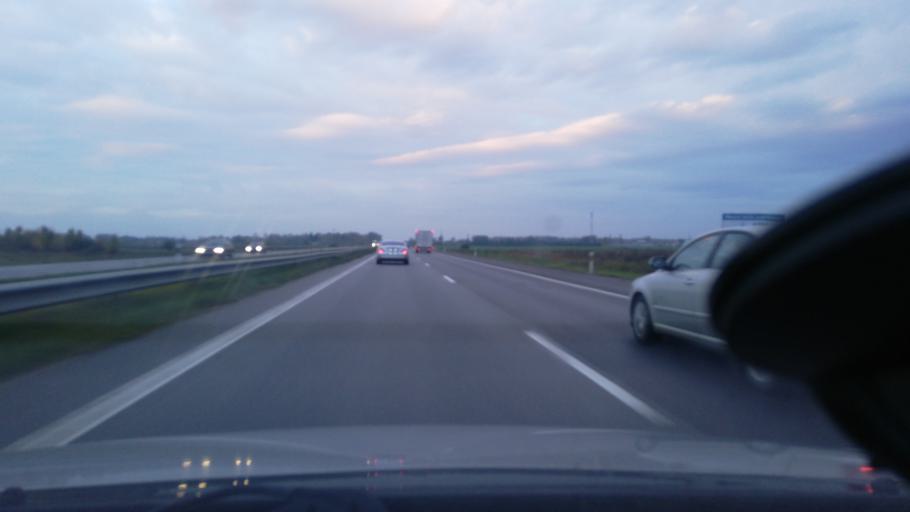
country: LT
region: Klaipedos apskritis
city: Gargzdai
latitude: 55.7263
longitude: 21.3306
